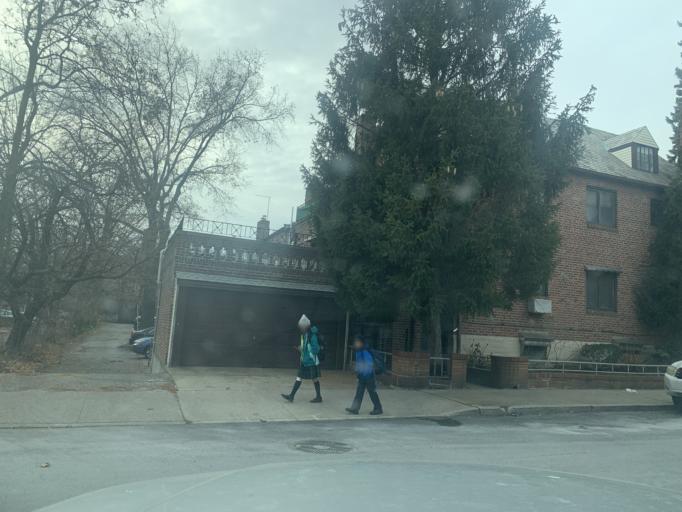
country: US
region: New York
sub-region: Queens County
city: Borough of Queens
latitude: 40.7278
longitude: -73.8692
